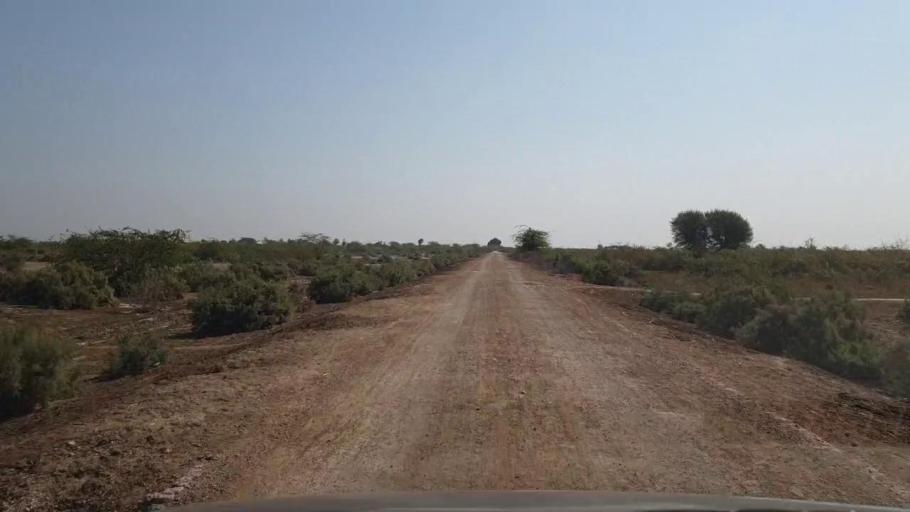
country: PK
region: Sindh
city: Samaro
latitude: 25.2486
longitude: 69.2835
